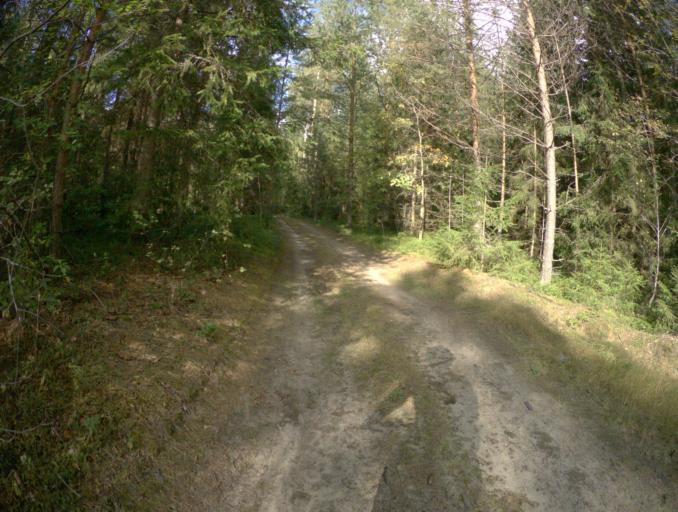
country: RU
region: Vladimir
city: Kommunar
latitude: 56.0274
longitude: 40.5214
